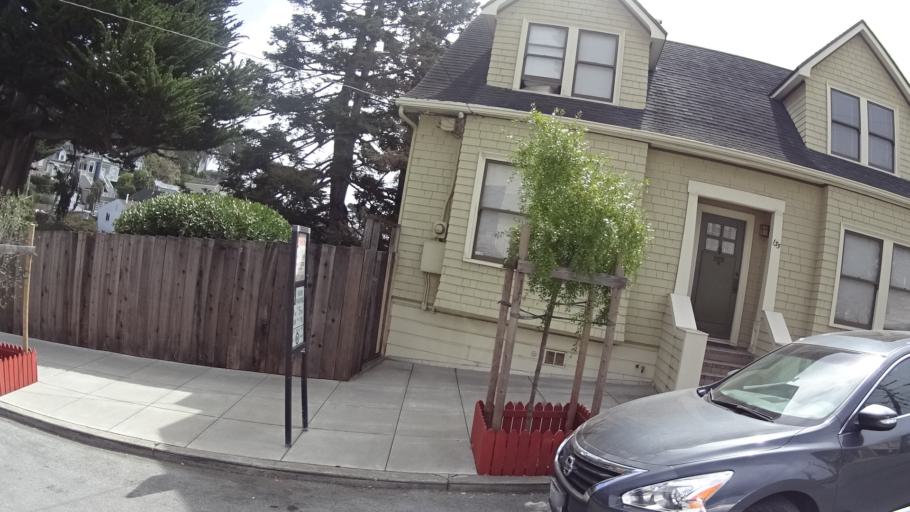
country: US
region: California
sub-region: San Mateo County
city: Daly City
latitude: 37.7369
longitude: -122.4353
